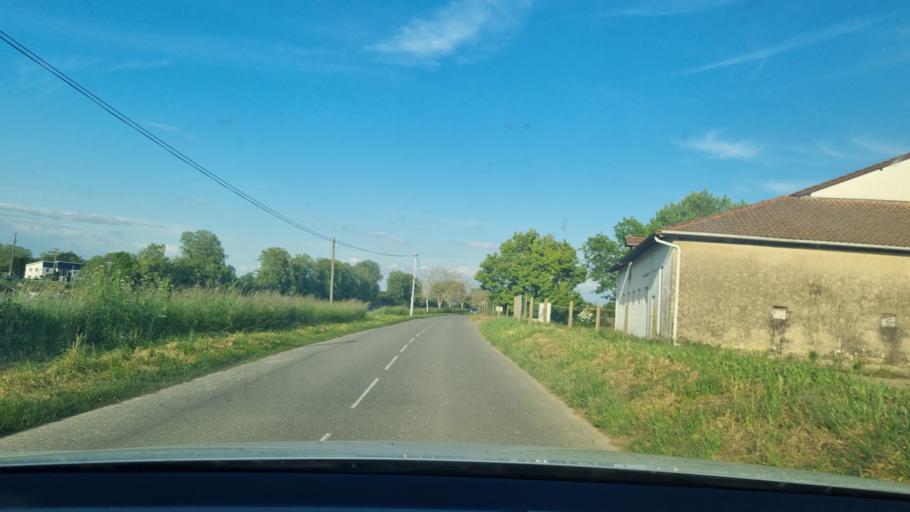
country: FR
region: Aquitaine
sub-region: Departement des Landes
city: Peyrehorade
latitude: 43.5466
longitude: -1.1896
